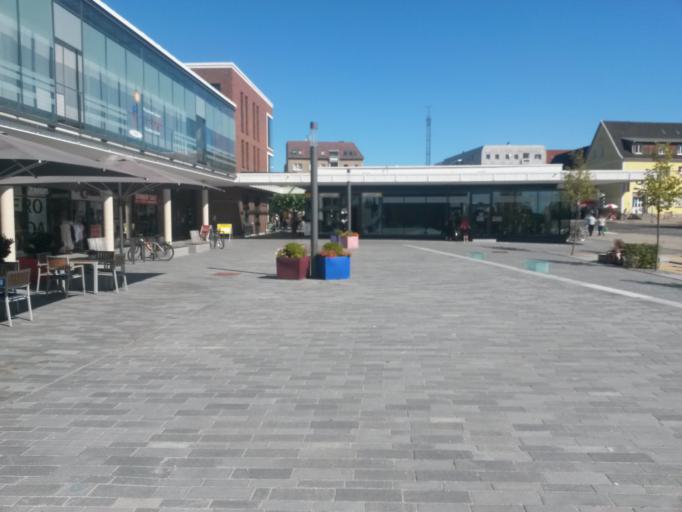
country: DE
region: Brandenburg
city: Prenzlau
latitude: 53.3137
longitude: 13.8586
